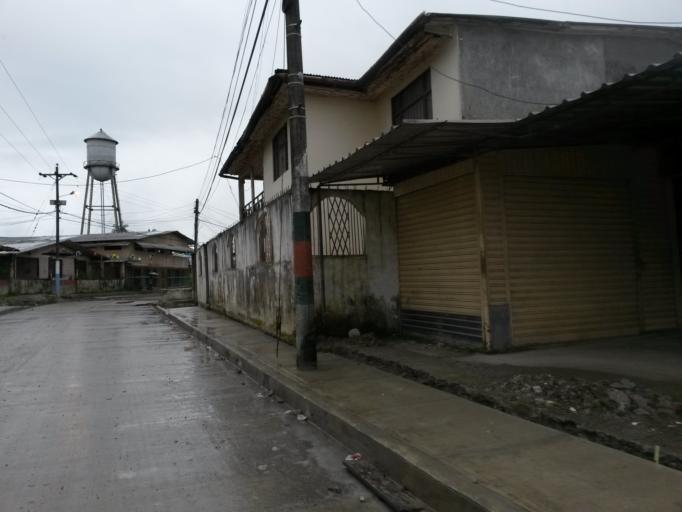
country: CO
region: Cauca
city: Guapi
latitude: 2.5727
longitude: -77.8892
